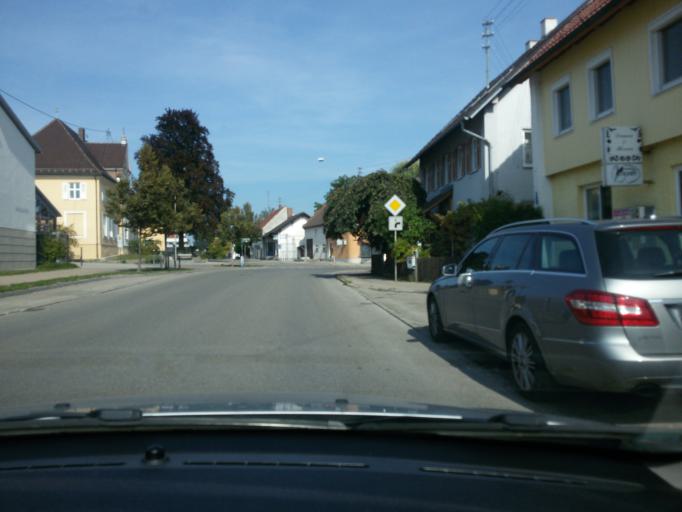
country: DE
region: Bavaria
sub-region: Swabia
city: Ziemetshausen
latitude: 48.2933
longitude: 10.5321
